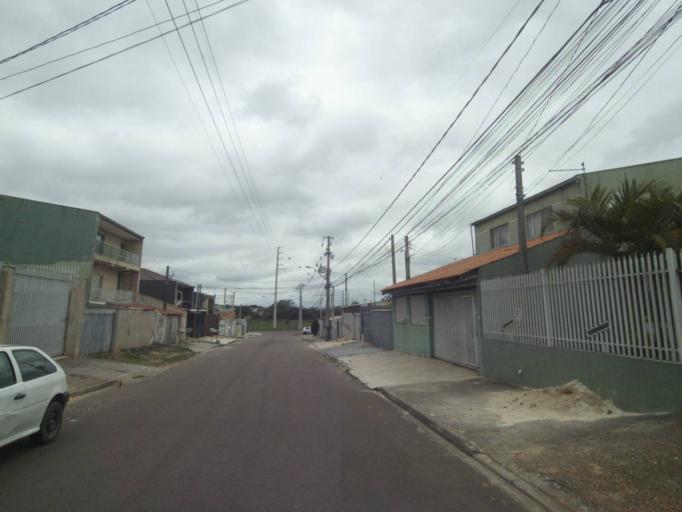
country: BR
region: Parana
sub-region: Sao Jose Dos Pinhais
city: Sao Jose dos Pinhais
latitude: -25.5502
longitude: -49.2573
